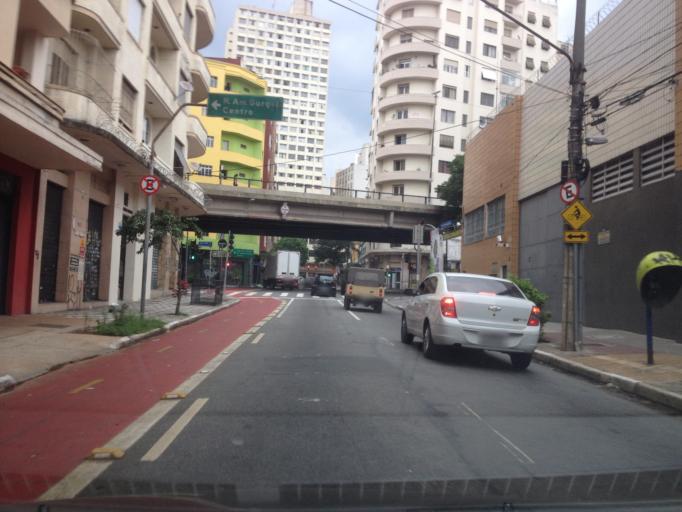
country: BR
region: Sao Paulo
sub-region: Sao Paulo
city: Sao Paulo
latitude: -23.5357
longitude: -46.6510
